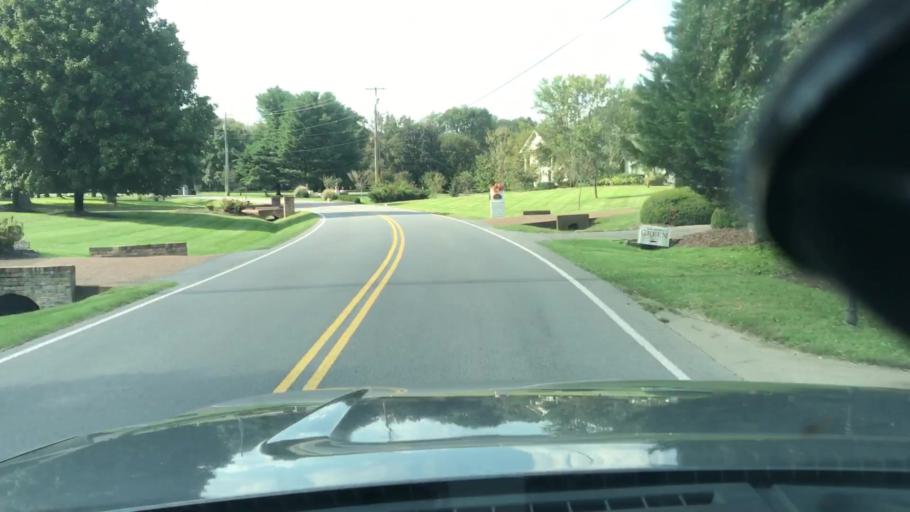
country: US
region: Tennessee
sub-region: Davidson County
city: Forest Hills
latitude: 36.0308
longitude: -86.8317
